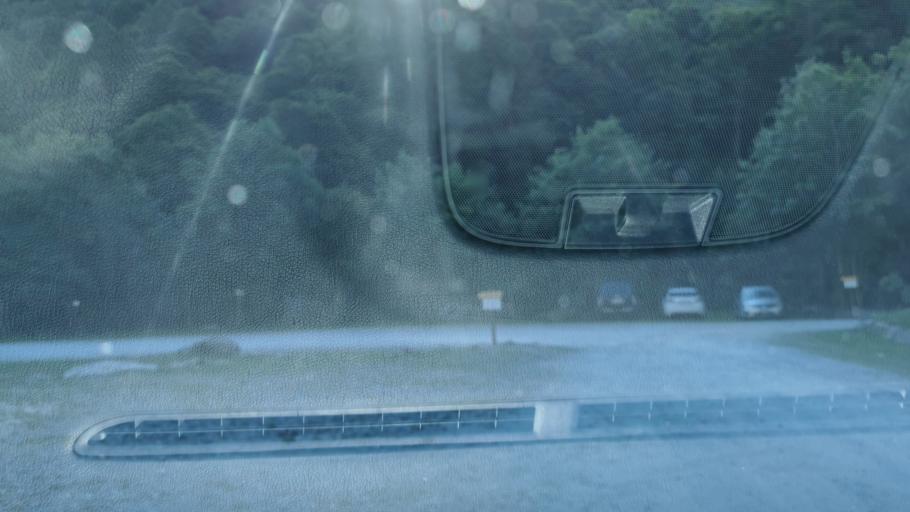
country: IT
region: Piedmont
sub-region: Provincia di Cuneo
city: Demonte
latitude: 44.2047
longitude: 7.2696
